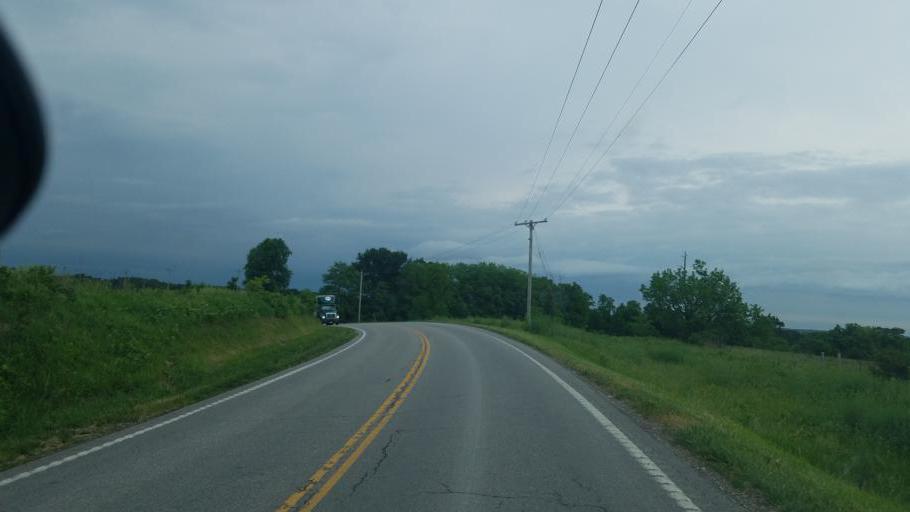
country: US
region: Missouri
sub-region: Cooper County
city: Boonville
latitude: 38.8699
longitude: -92.6411
